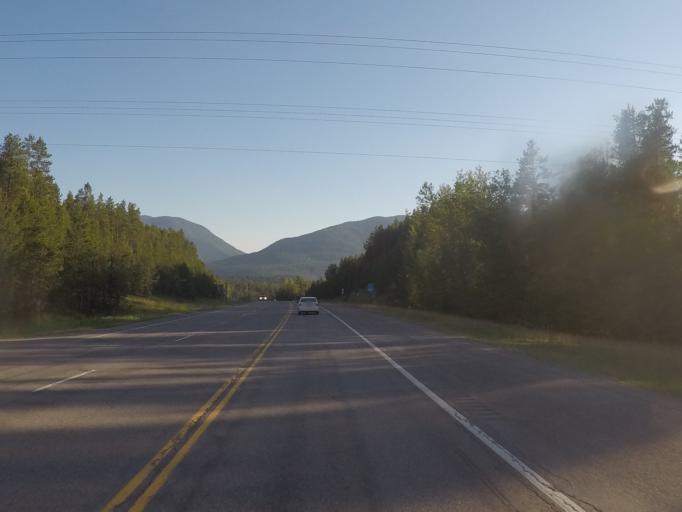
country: US
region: Montana
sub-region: Flathead County
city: Columbia Falls
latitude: 48.4452
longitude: -114.0359
